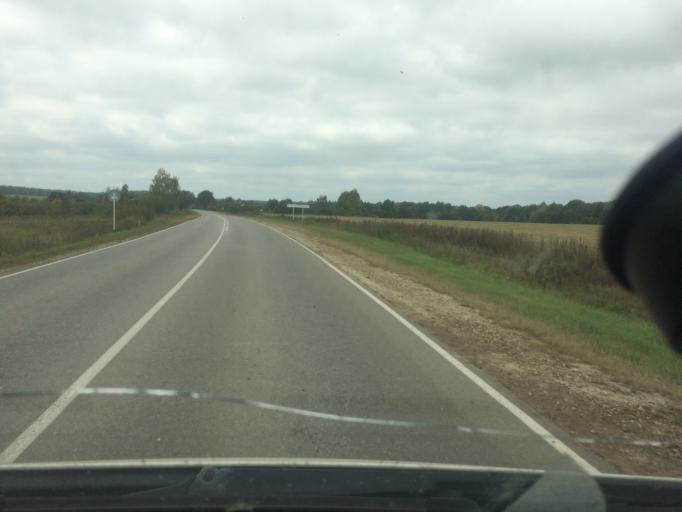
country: RU
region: Tula
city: Odoyev
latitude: 53.9983
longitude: 36.6798
